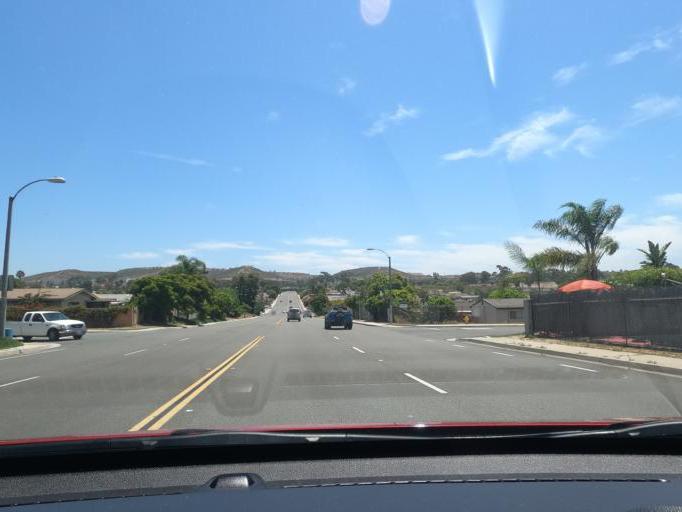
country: US
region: California
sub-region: San Diego County
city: Imperial Beach
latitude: 32.5736
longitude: -117.0458
